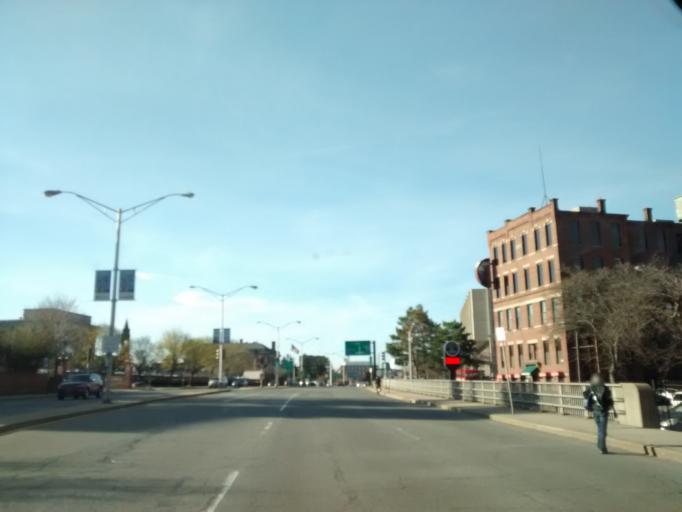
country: US
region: Massachusetts
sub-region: Worcester County
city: Worcester
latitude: 42.2693
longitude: -71.7986
